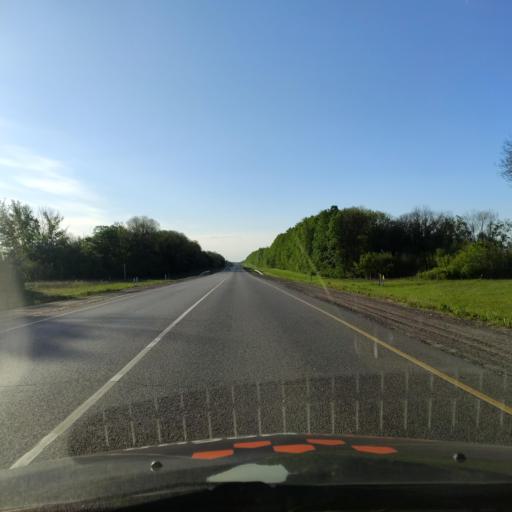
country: RU
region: Lipetsk
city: Yelets
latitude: 52.5726
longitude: 38.6560
